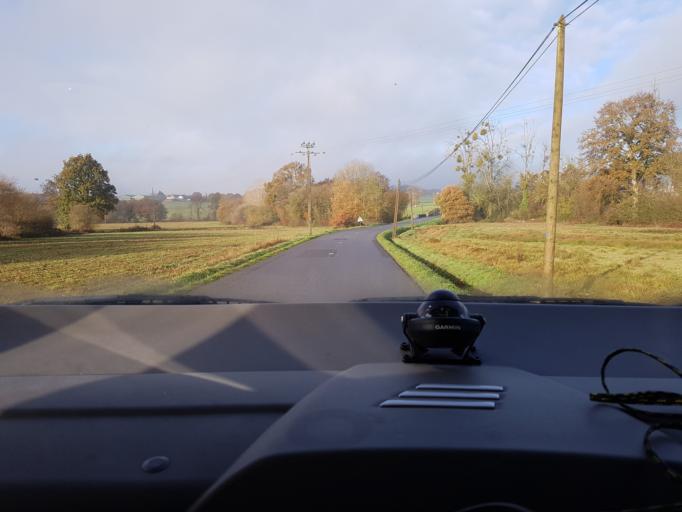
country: FR
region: Brittany
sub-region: Departement d'Ille-et-Vilaine
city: Liffre
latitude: 48.1822
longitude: -1.4970
